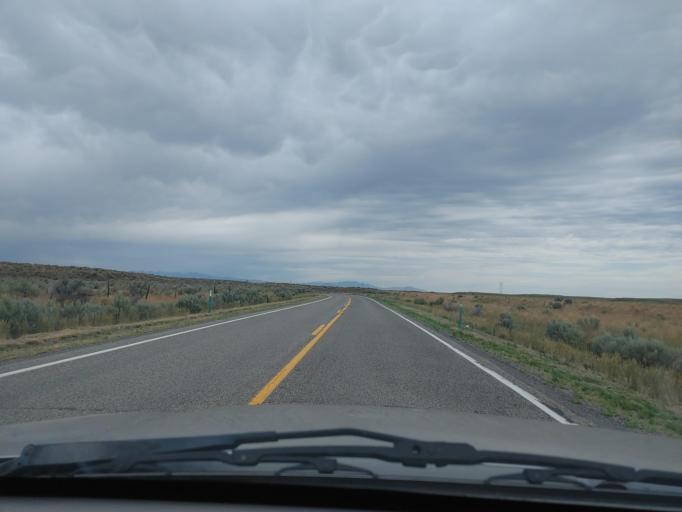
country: US
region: Idaho
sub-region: Lincoln County
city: Shoshone
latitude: 43.0774
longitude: -114.1031
